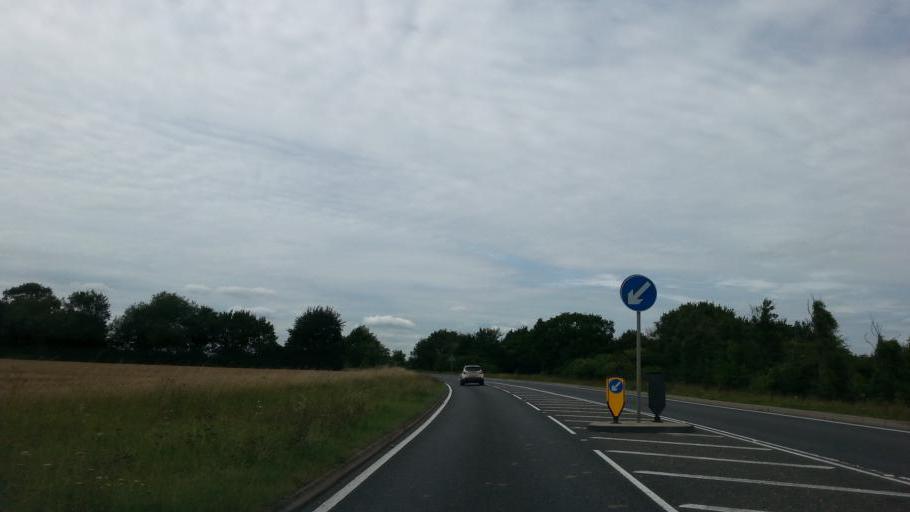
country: GB
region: England
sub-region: Essex
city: Chelmsford
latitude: 51.8200
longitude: 0.4459
